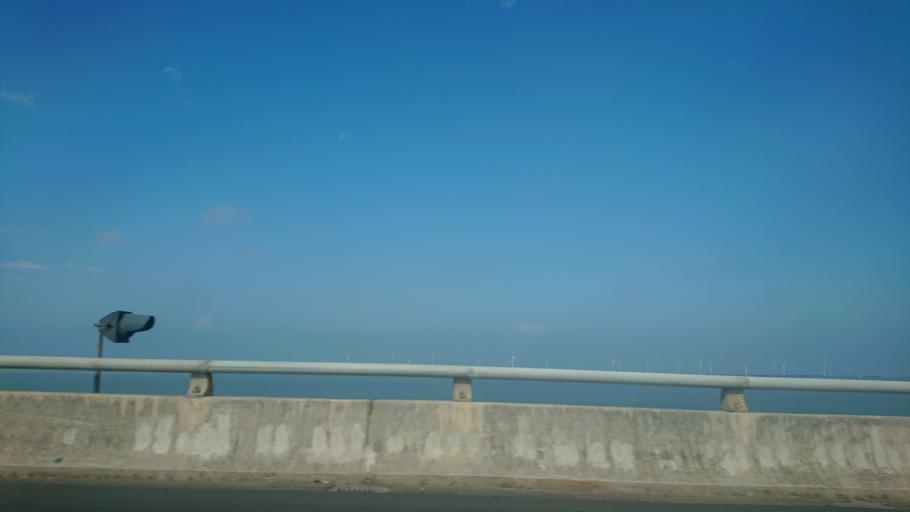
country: TW
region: Taiwan
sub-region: Changhua
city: Chang-hua
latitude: 24.0891
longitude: 120.4288
